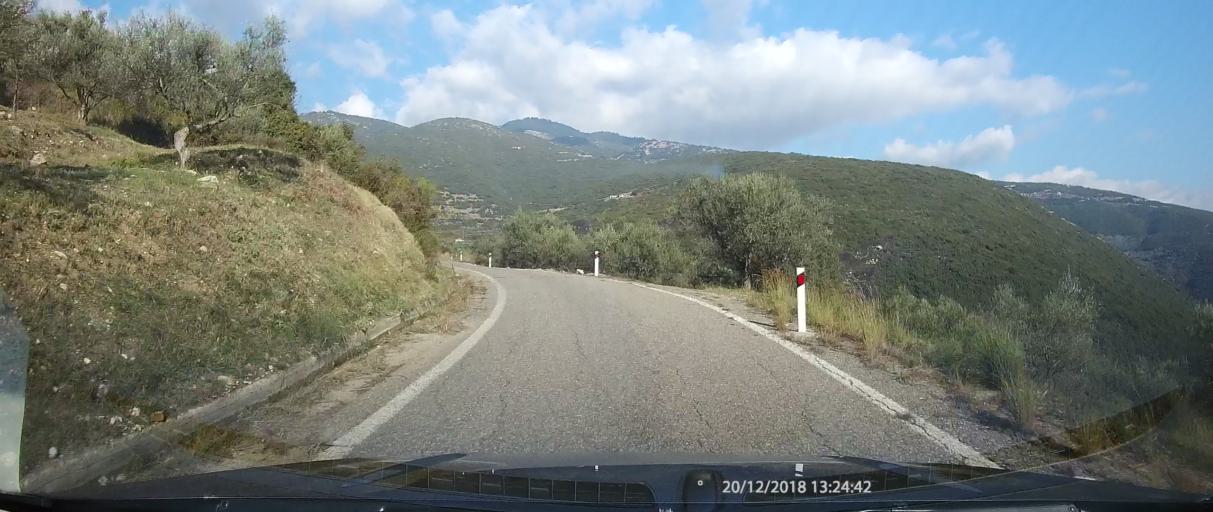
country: GR
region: West Greece
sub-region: Nomos Aitolias kai Akarnanias
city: Paravola
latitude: 38.6203
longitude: 21.5676
